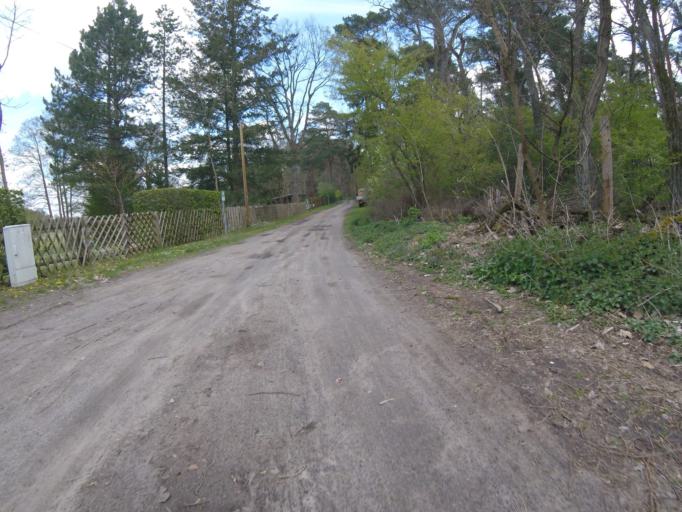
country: DE
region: Brandenburg
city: Gross Koris
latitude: 52.2168
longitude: 13.7610
